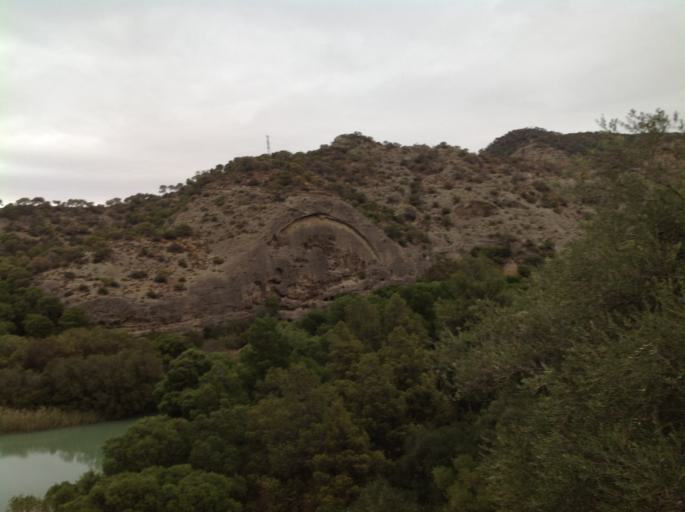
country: ES
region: Andalusia
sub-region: Provincia de Malaga
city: Ardales
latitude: 36.9298
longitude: -4.7925
